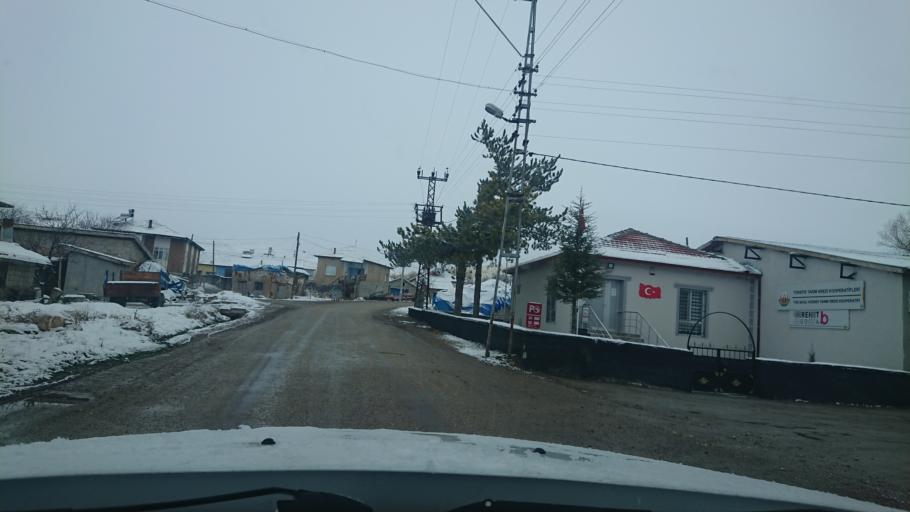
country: TR
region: Aksaray
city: Agacoren
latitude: 38.7580
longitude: 33.8688
